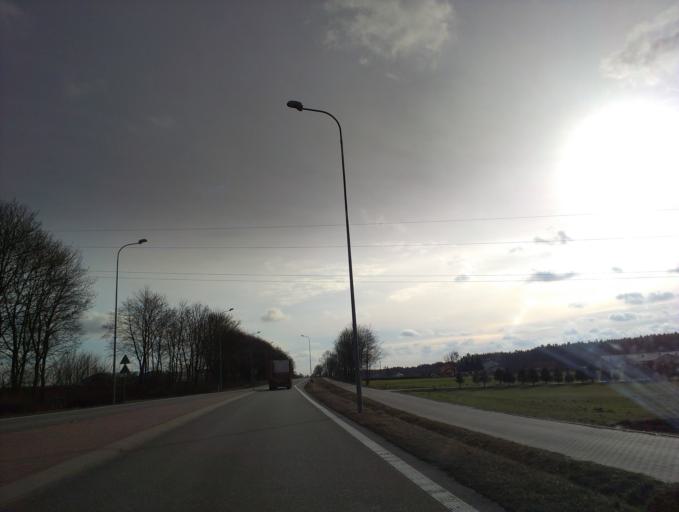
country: PL
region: Kujawsko-Pomorskie
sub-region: Powiat lipnowski
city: Lipno
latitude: 52.8697
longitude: 19.1532
